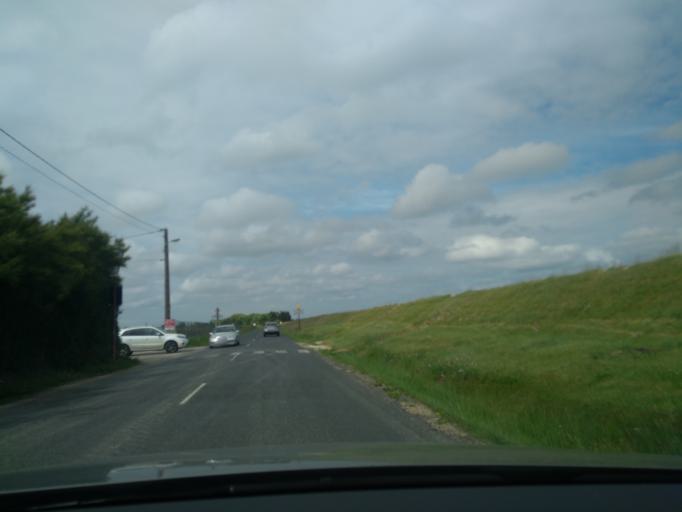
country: FR
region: Lower Normandy
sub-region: Departement de la Manche
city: Saint-Vaast-la-Hougue
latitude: 49.5963
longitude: -1.2646
